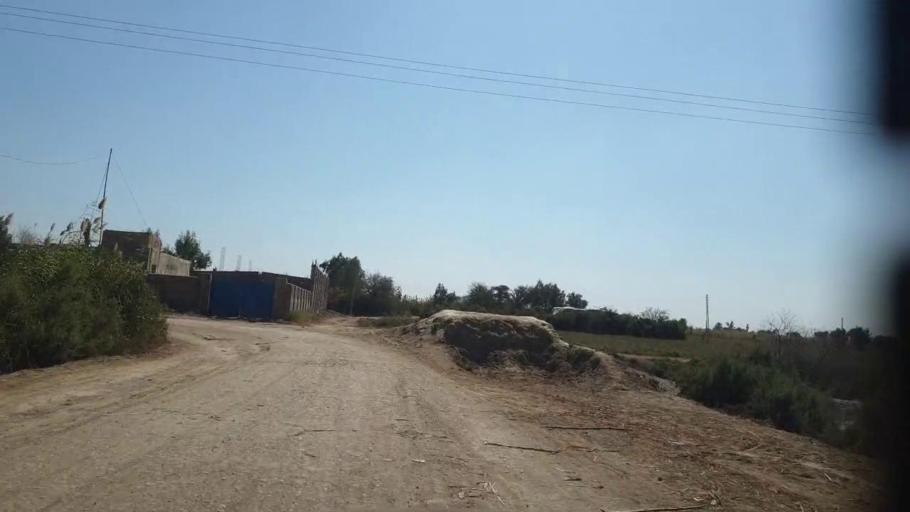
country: PK
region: Sindh
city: Mirpur Khas
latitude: 25.5939
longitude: 69.1052
